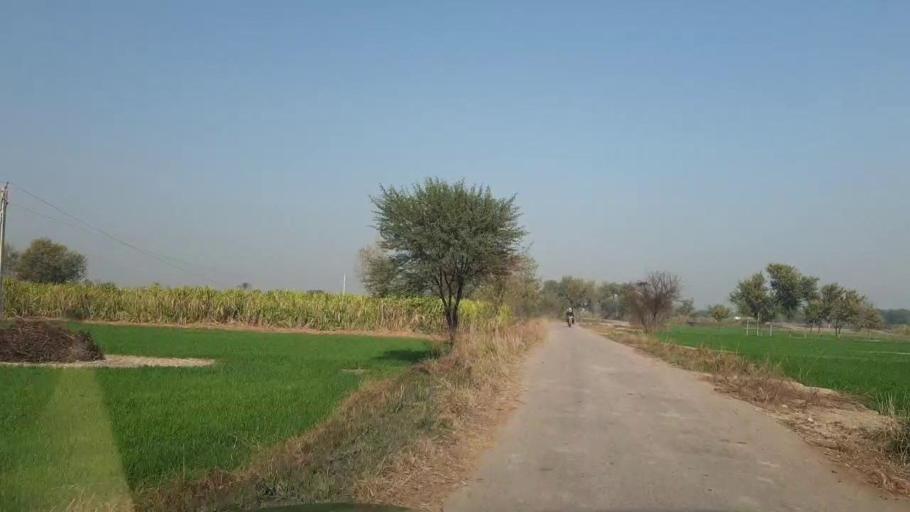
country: PK
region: Sindh
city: Ubauro
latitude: 28.1335
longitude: 69.7695
